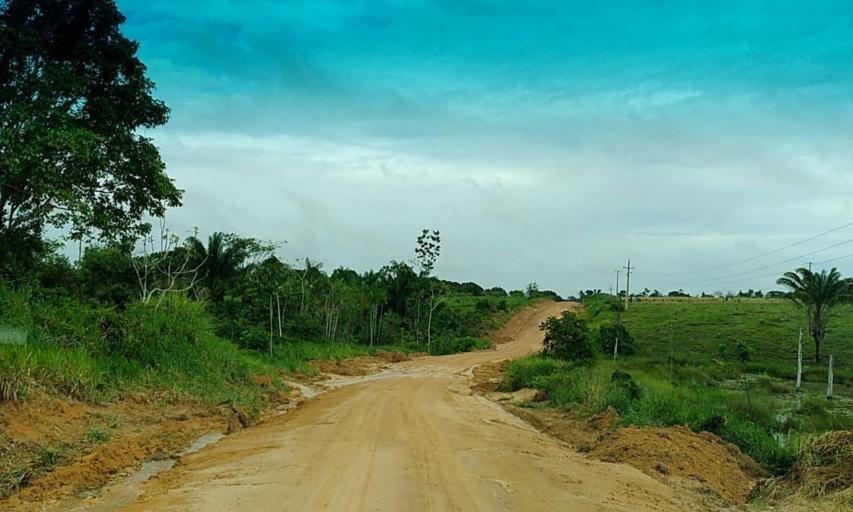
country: BR
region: Para
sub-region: Senador Jose Porfirio
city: Senador Jose Porfirio
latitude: -3.0326
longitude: -51.6813
